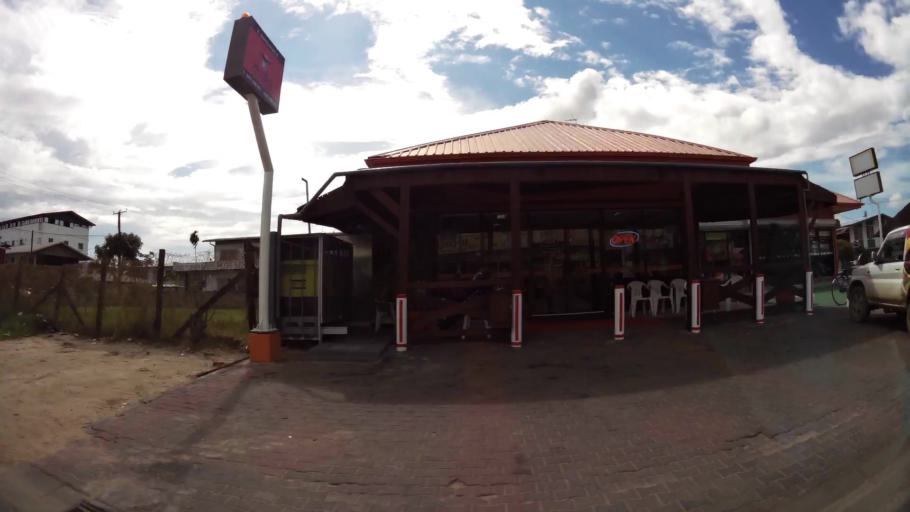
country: SR
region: Paramaribo
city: Paramaribo
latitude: 5.8486
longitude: -55.1463
